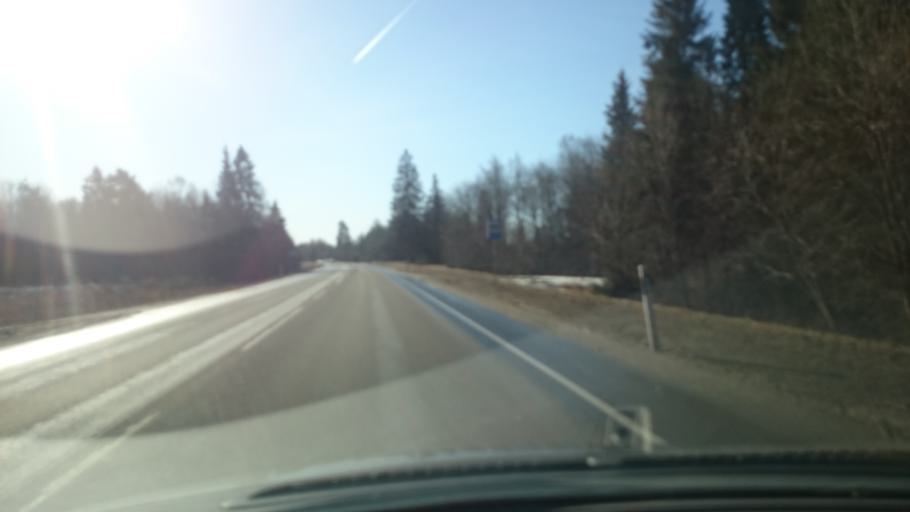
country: EE
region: Raplamaa
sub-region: Kohila vald
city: Kohila
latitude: 59.2456
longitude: 24.7492
